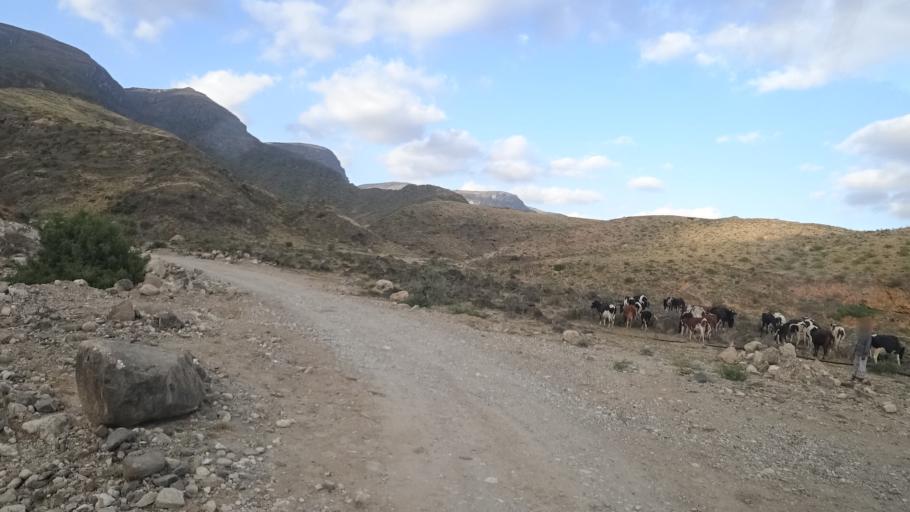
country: OM
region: Zufar
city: Salalah
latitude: 16.9951
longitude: 53.8461
